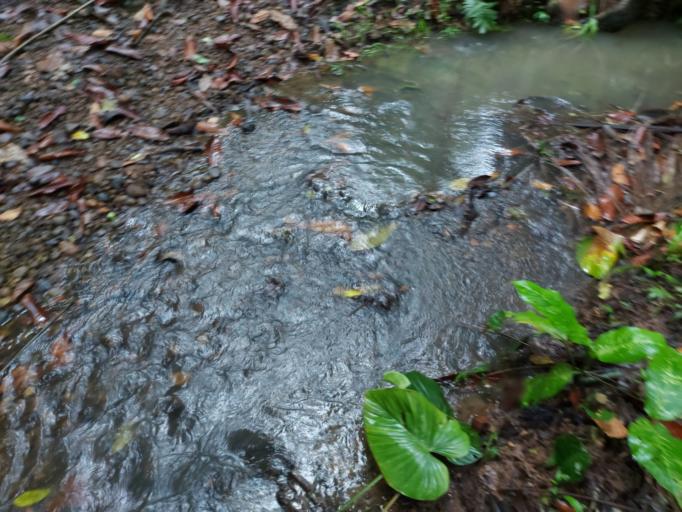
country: PA
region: Bocas del Toro
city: Barranco
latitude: 9.6302
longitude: -82.7777
